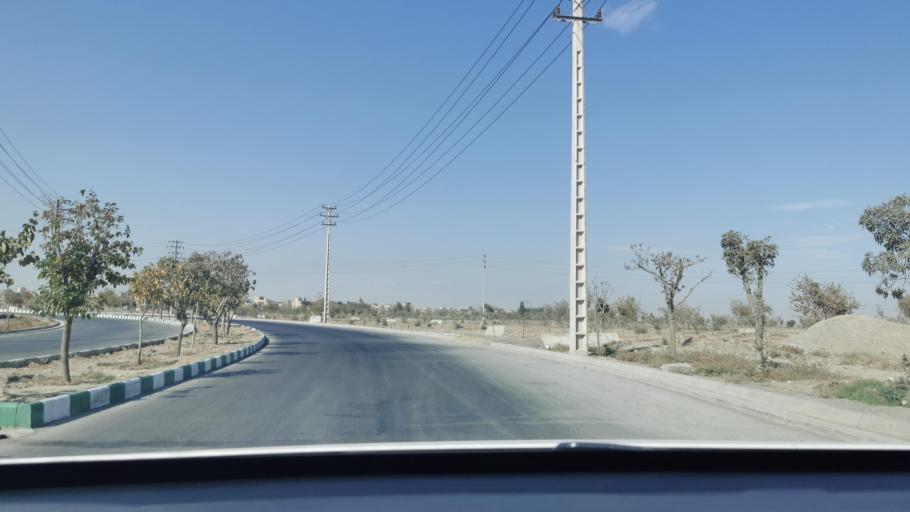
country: IR
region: Razavi Khorasan
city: Mashhad
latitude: 36.3471
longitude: 59.6114
